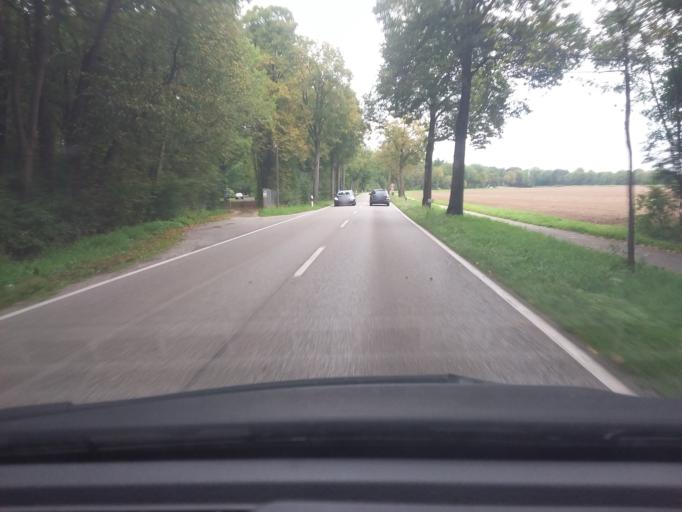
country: DE
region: Bavaria
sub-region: Upper Bavaria
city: Oberschleissheim
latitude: 48.2356
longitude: 11.5419
